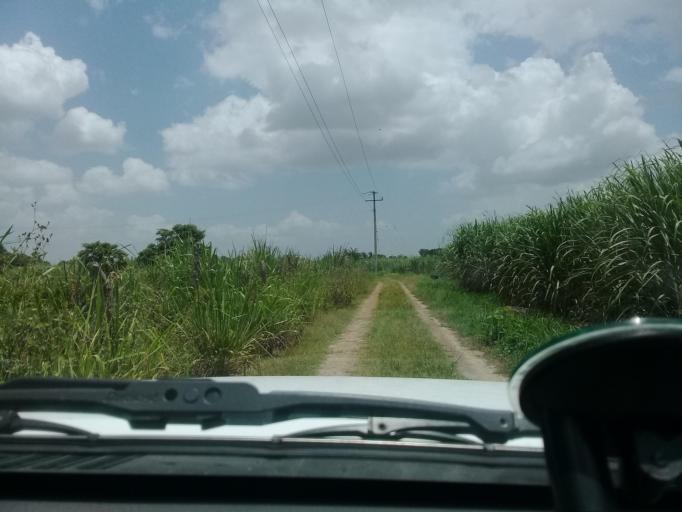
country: MX
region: Veracruz
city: Moralillo
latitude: 22.1342
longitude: -98.0385
